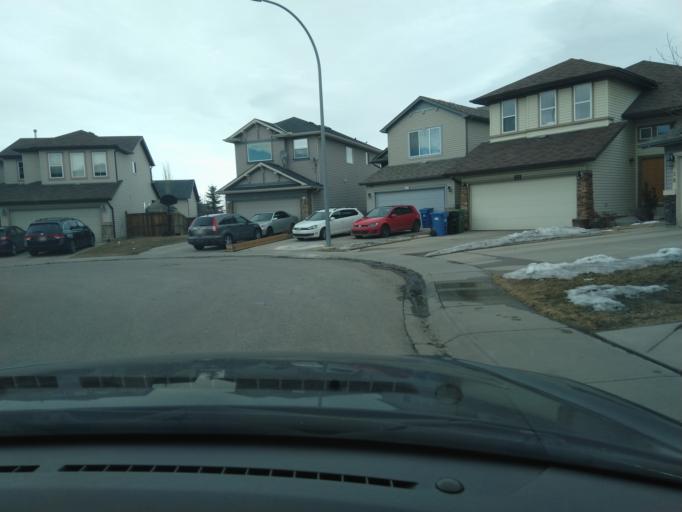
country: CA
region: Alberta
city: Calgary
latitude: 51.1589
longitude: -114.0879
